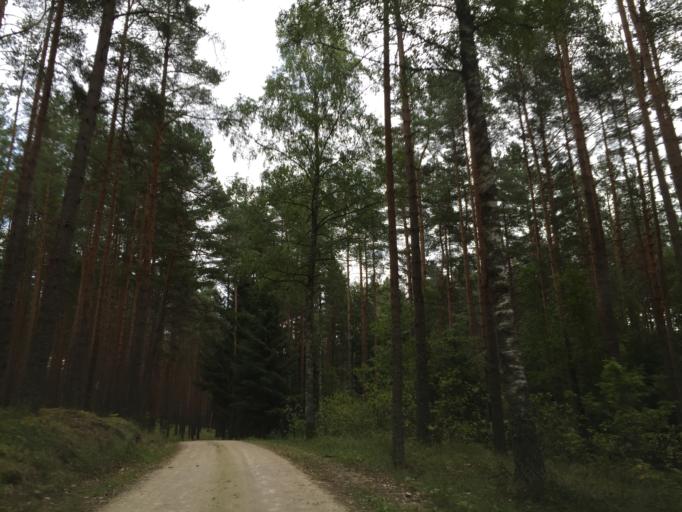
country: LV
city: Tireli
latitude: 56.8657
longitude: 23.6628
